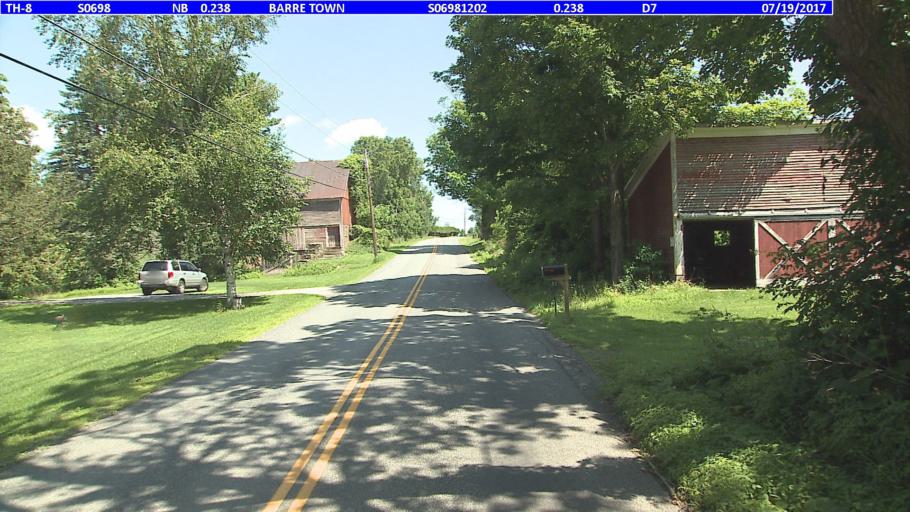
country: US
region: Vermont
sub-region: Washington County
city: Barre
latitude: 44.2225
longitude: -72.4610
